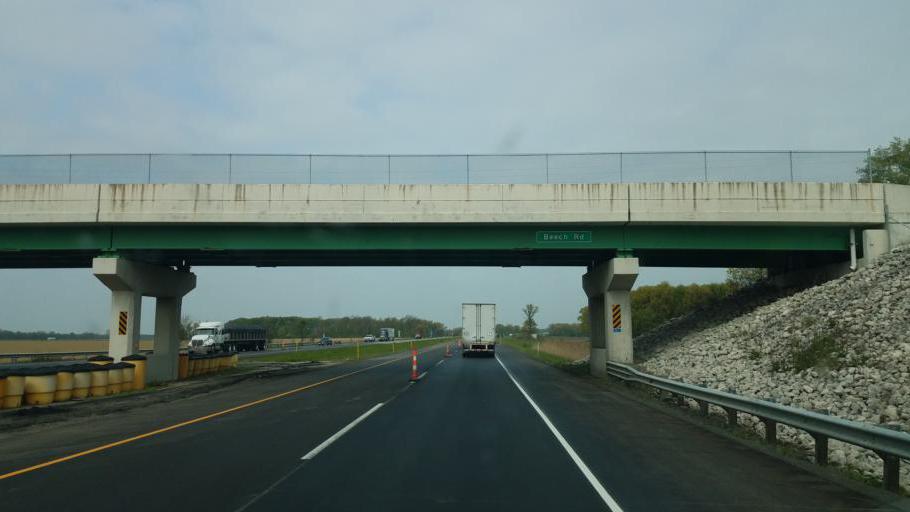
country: US
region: Indiana
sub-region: Saint Joseph County
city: Granger
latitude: 41.7314
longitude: -86.0808
